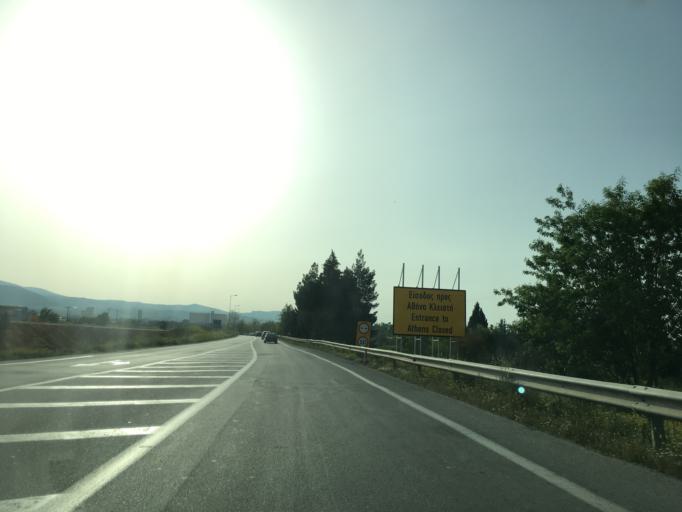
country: GR
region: Thessaly
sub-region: Nomos Magnisias
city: Velestino
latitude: 39.3871
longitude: 22.7852
